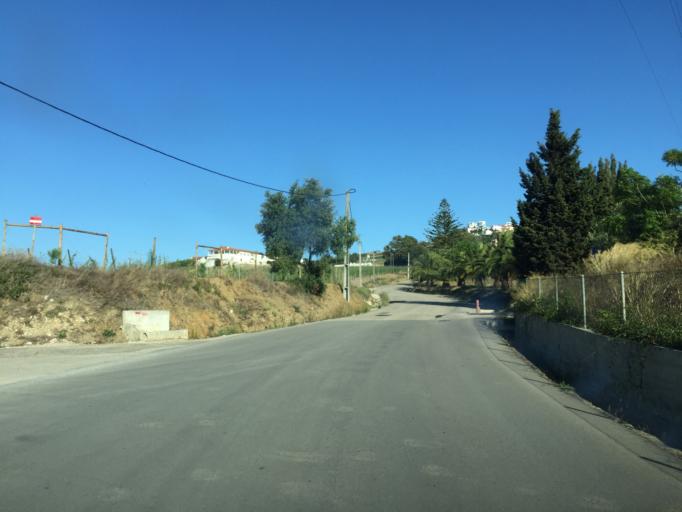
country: PT
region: Lisbon
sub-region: Torres Vedras
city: Torres Vedras
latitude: 39.0947
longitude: -9.2842
